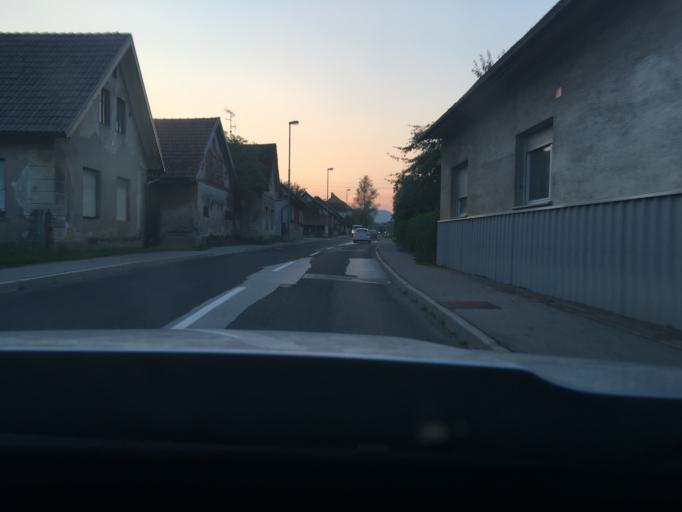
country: SI
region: Ribnica
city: Ribnica
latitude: 45.7438
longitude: 14.7224
